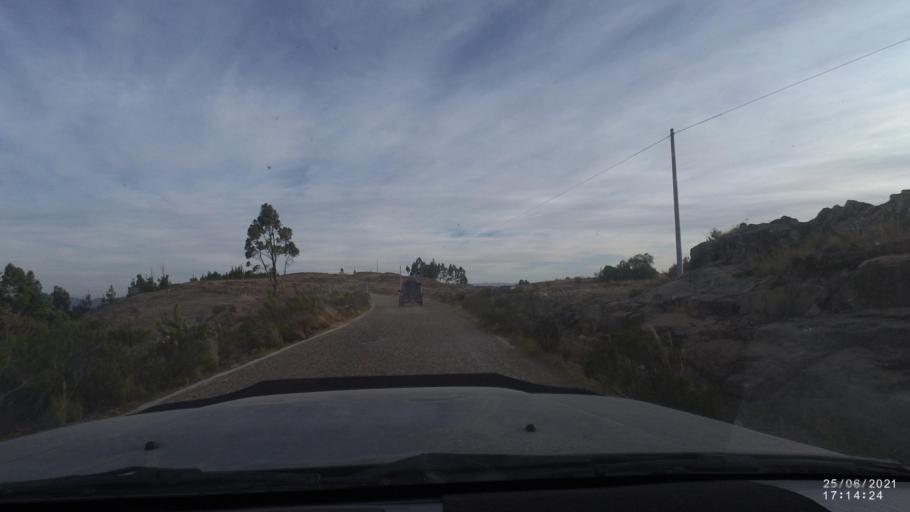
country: BO
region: Cochabamba
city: Arani
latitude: -17.8664
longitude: -65.6974
